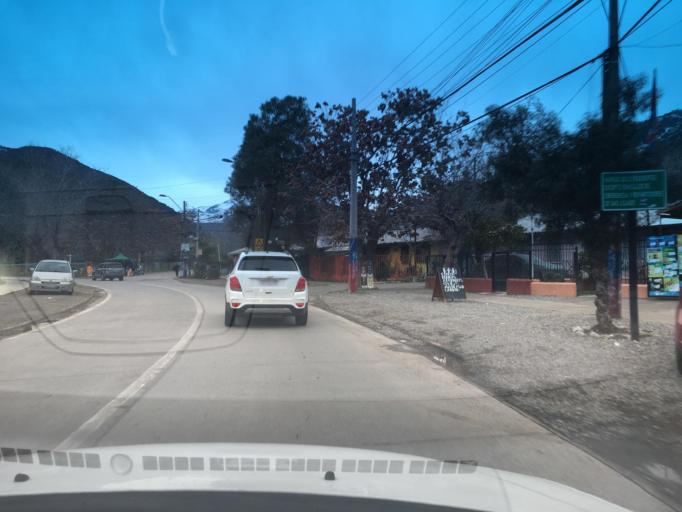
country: CL
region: Santiago Metropolitan
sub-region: Provincia de Cordillera
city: Puente Alto
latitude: -33.6446
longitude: -70.3528
